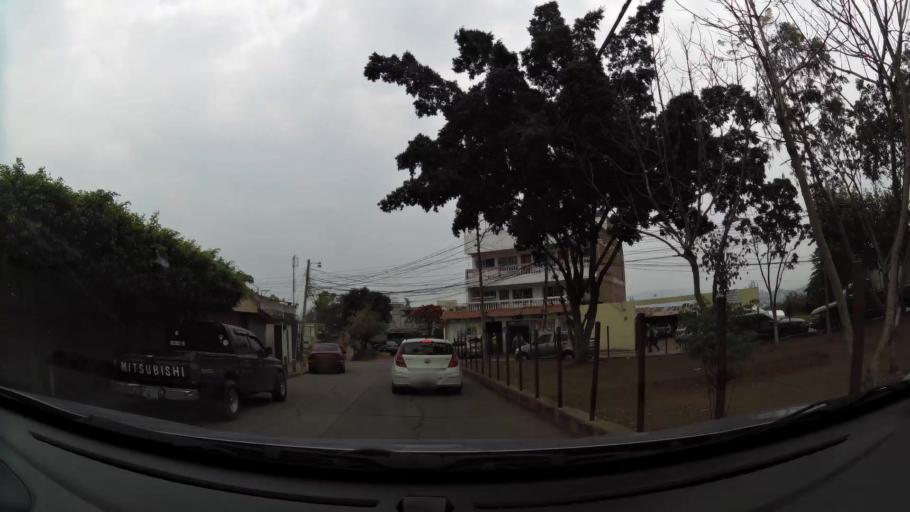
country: HN
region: Francisco Morazan
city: Tegucigalpa
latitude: 14.0741
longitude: -87.1728
